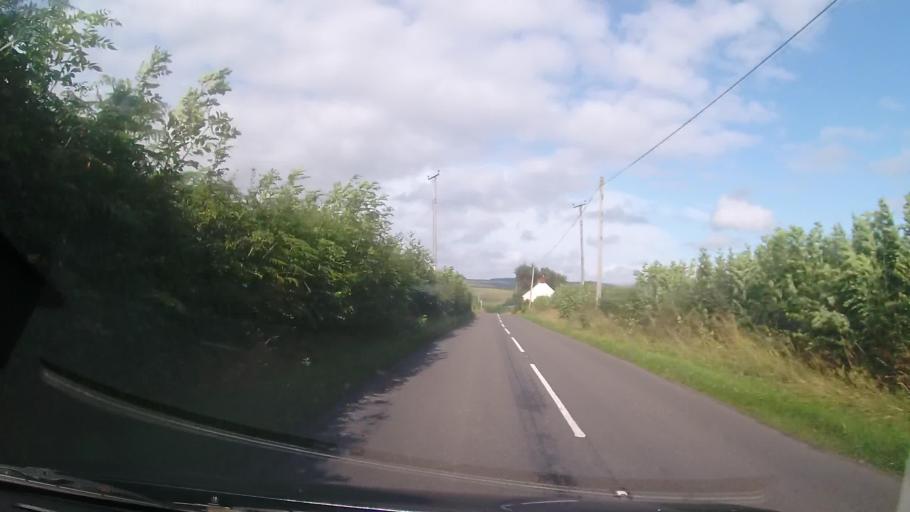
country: GB
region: Wales
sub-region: Sir Powys
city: Knighton
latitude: 52.3775
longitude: -3.0456
